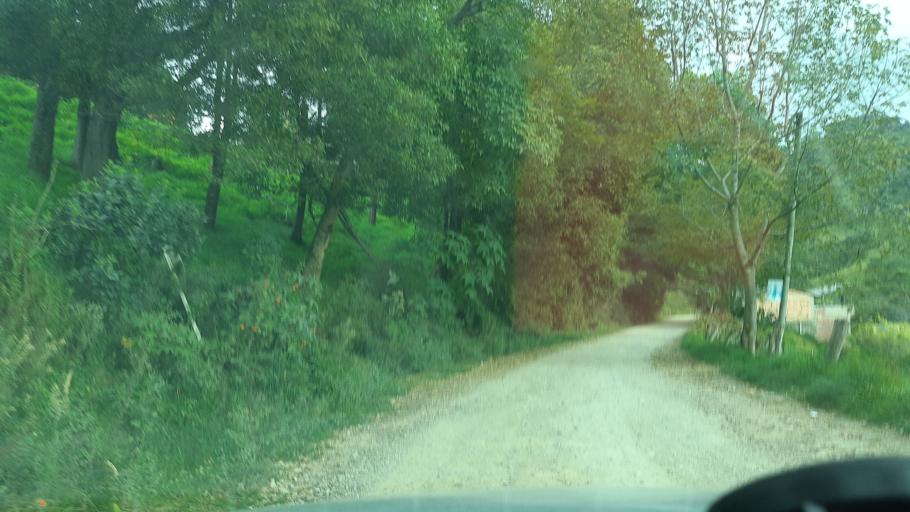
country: CO
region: Boyaca
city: Santa Sofia
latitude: 5.7501
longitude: -73.5488
